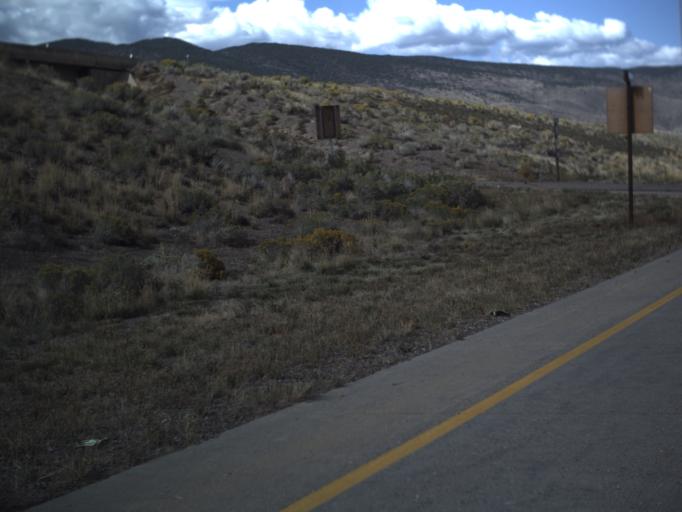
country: US
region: Utah
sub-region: Sevier County
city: Monroe
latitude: 38.6242
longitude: -112.2256
